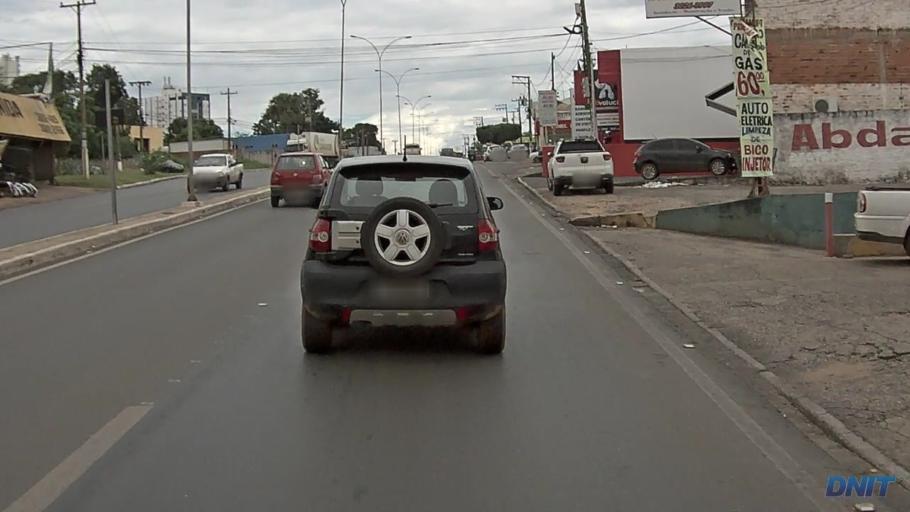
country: BR
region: Mato Grosso
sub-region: Varzea Grande
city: Varzea Grande
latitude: -15.6437
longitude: -56.1366
